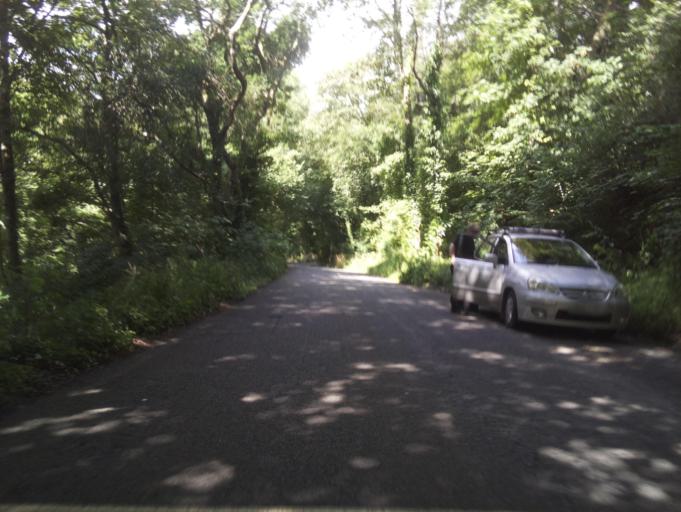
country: GB
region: England
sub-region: Devon
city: Dartmouth
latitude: 50.3553
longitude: -3.5626
